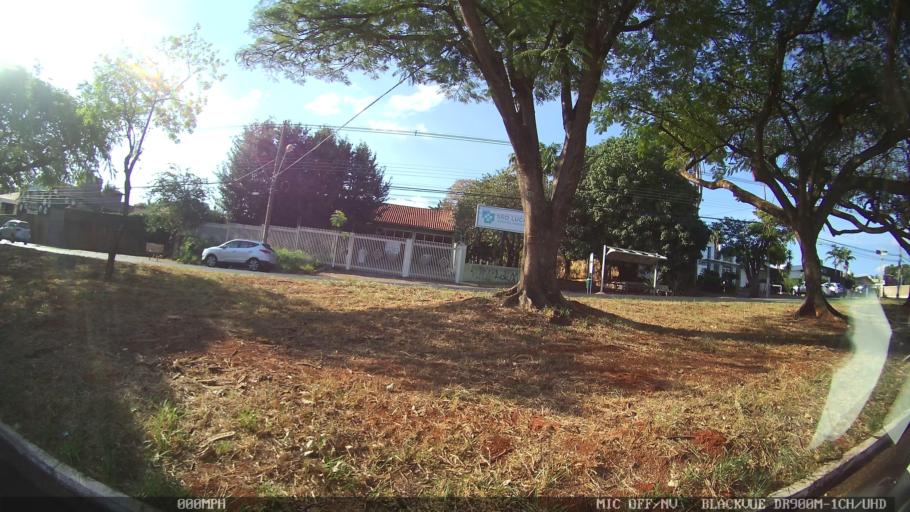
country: BR
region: Sao Paulo
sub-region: Ribeirao Preto
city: Ribeirao Preto
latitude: -21.2013
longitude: -47.7875
